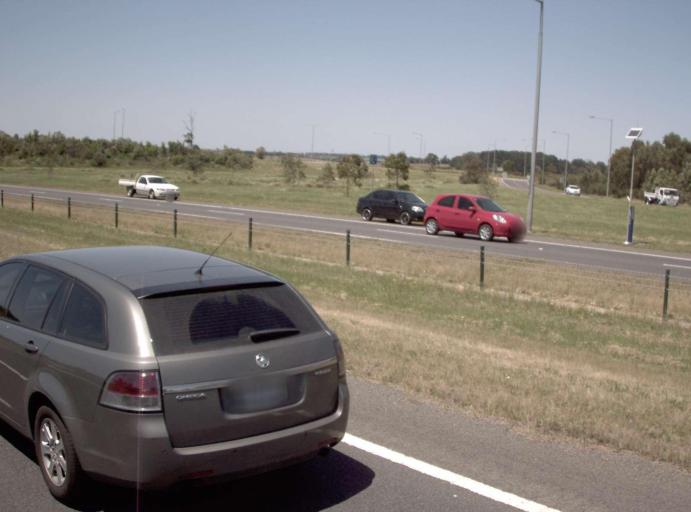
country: AU
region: Victoria
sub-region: Casey
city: Berwick
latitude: -38.0596
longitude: 145.3677
